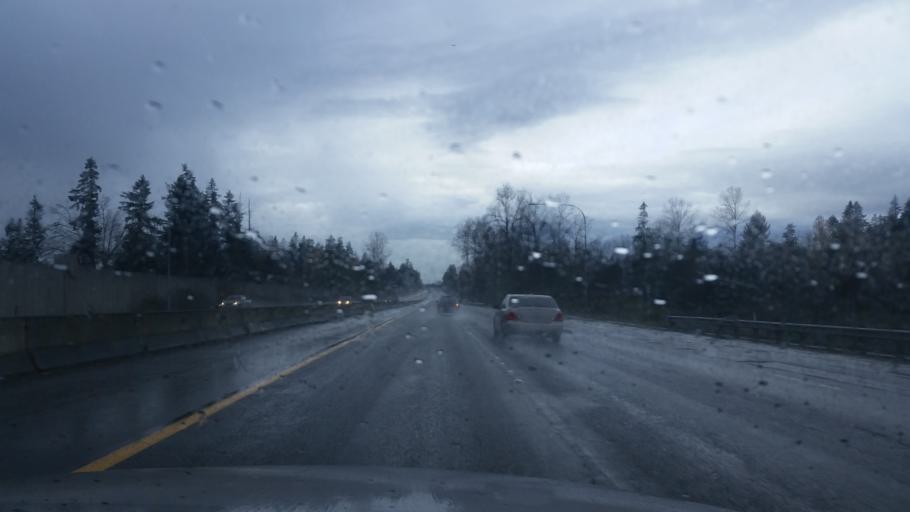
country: US
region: Washington
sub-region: King County
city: Covington
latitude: 47.3712
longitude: -122.0952
